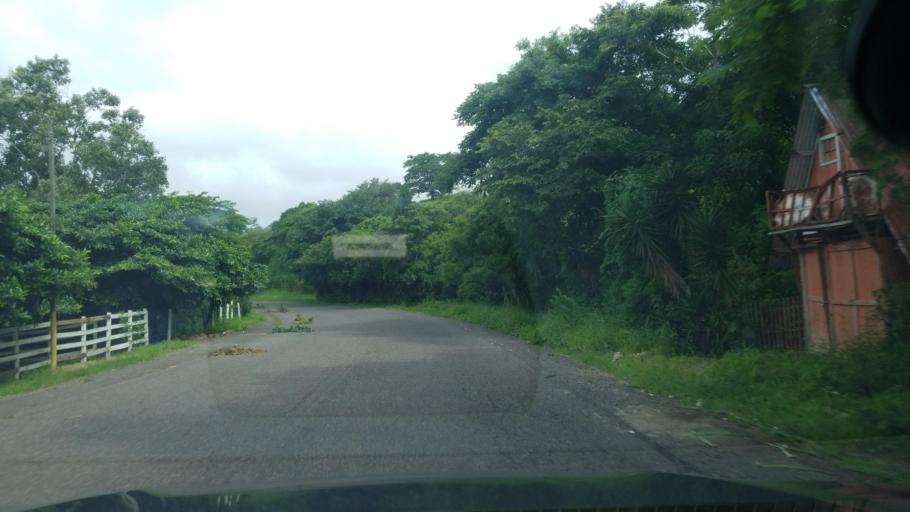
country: HN
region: Choluteca
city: Corpus
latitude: 13.3693
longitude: -86.9361
